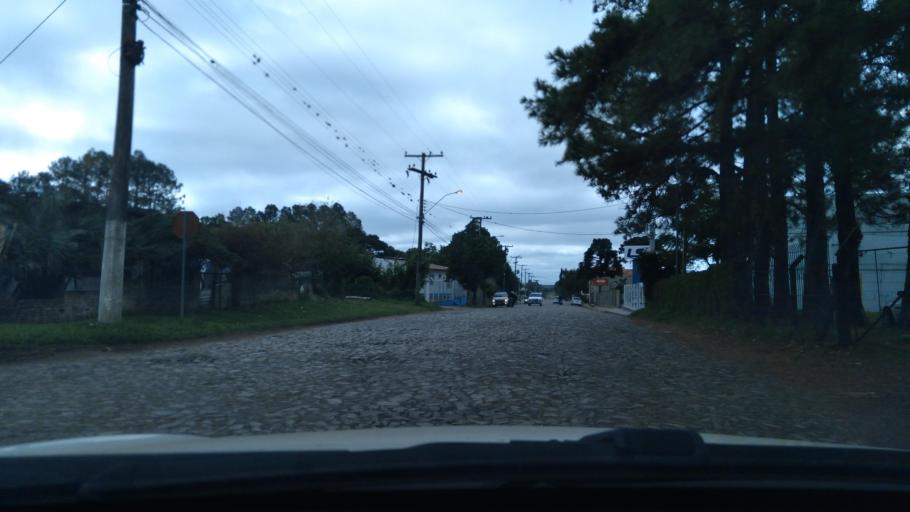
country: BR
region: Rio Grande do Sul
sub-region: Dom Pedrito
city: Dom Pedrito
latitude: -30.9670
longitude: -54.6735
